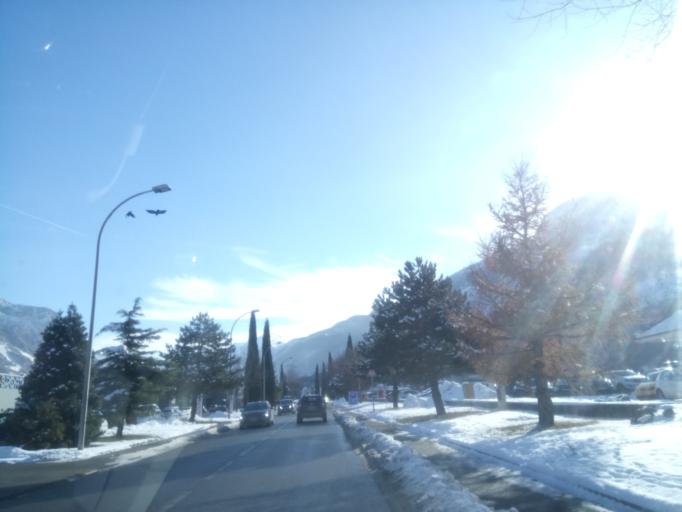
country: FR
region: Rhone-Alpes
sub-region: Departement de la Savoie
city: Villargondran
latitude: 45.2705
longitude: 6.3647
